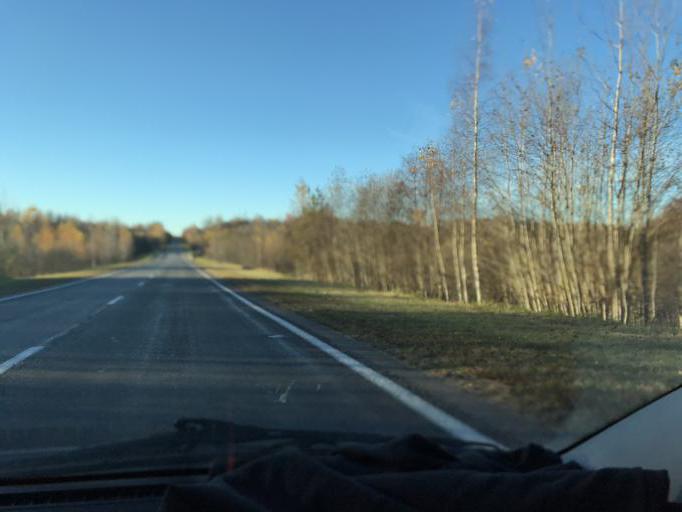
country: BY
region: Vitebsk
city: Vitebsk
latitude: 55.3511
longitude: 30.2005
